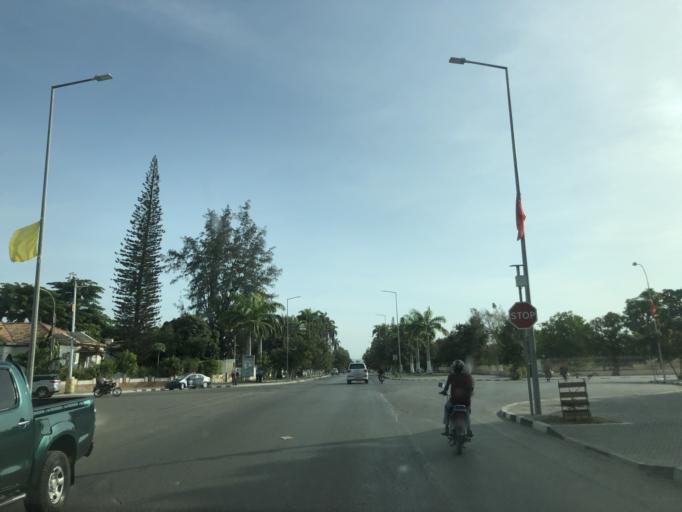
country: AO
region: Benguela
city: Benguela
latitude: -12.5778
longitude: 13.3995
